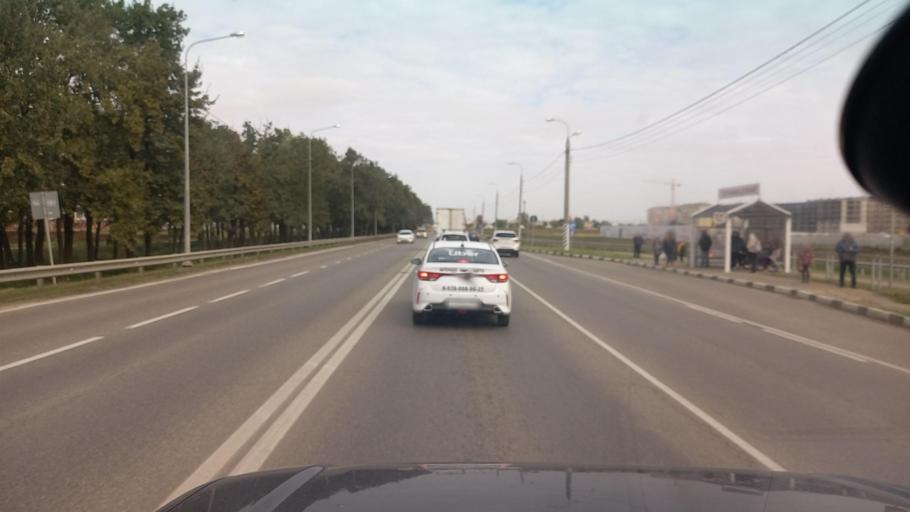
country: RU
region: Krasnodarskiy
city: Krasnodar
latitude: 45.0947
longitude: 38.9093
